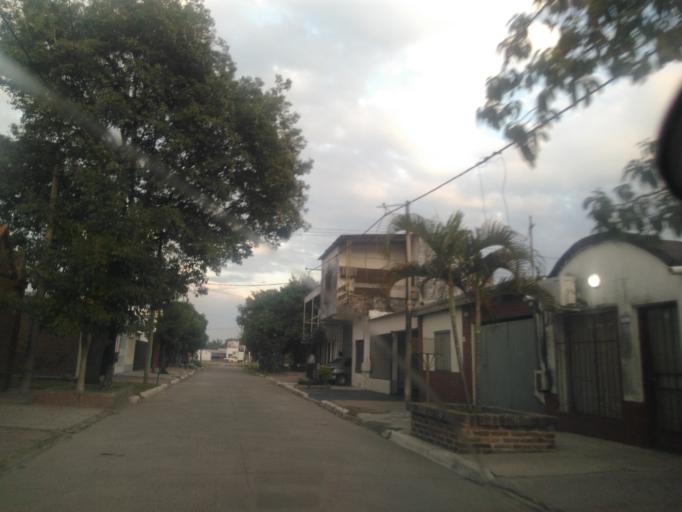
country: AR
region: Chaco
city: Resistencia
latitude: -27.4549
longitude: -59.0181
